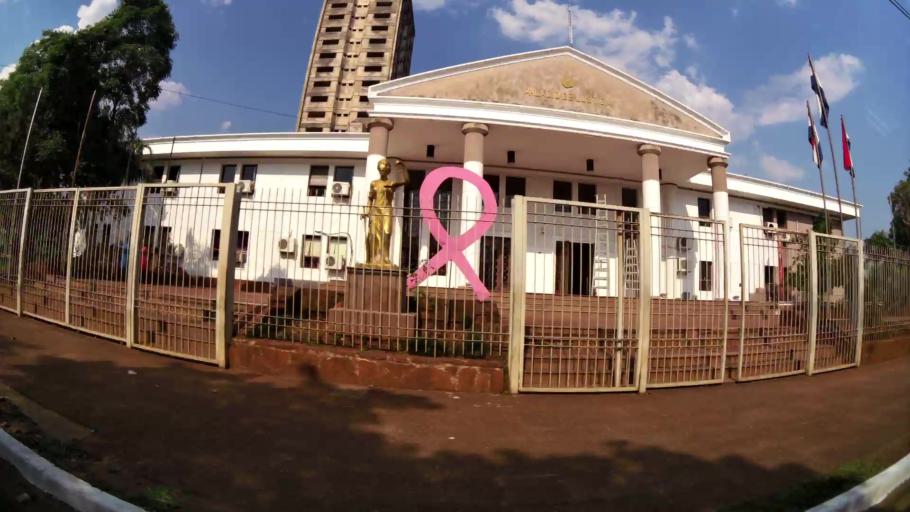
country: PY
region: Alto Parana
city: Presidente Franco
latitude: -25.5254
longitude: -54.6110
